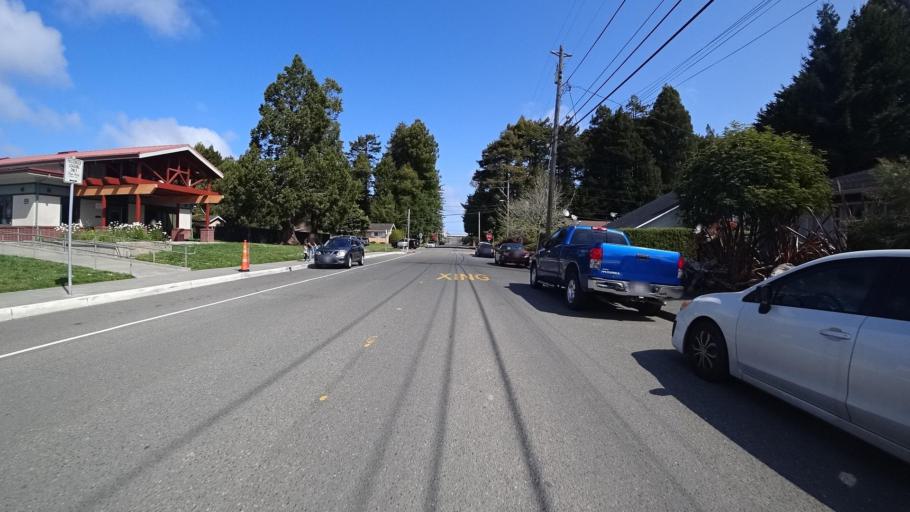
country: US
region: California
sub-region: Humboldt County
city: Cutten
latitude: 40.7781
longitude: -124.1421
